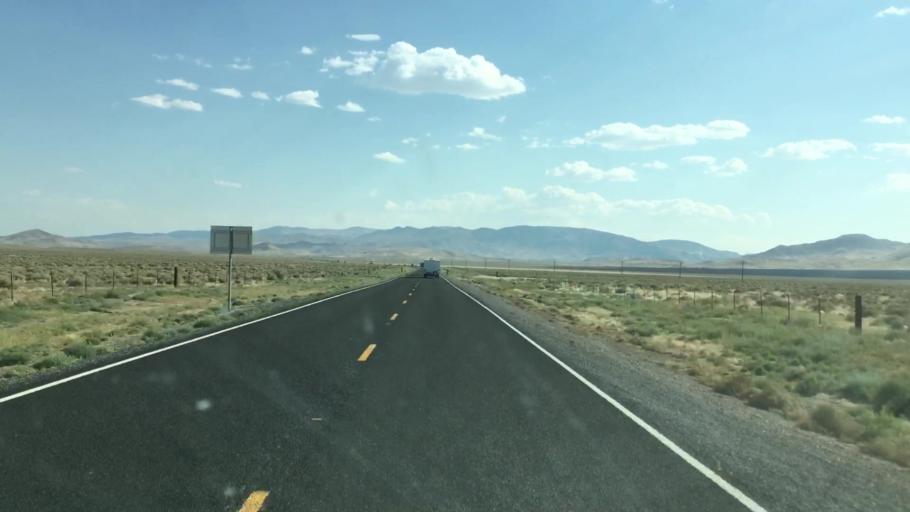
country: US
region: Nevada
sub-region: Lyon County
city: Fernley
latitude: 39.6917
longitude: -119.3352
